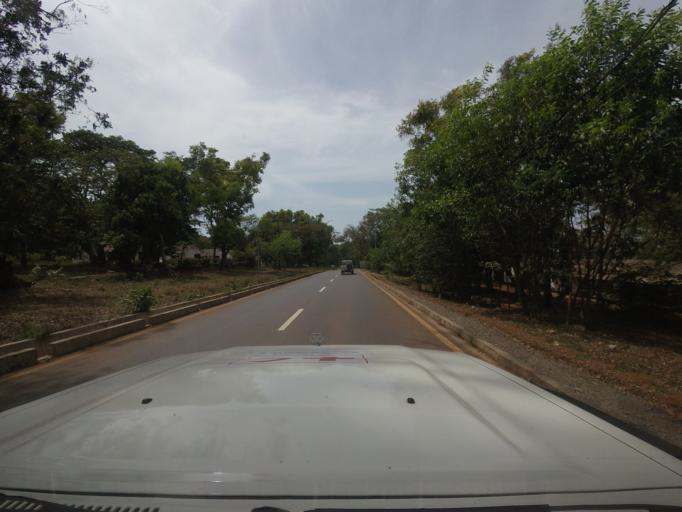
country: SL
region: Western Area
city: Freetown
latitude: 8.4696
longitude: -13.2145
